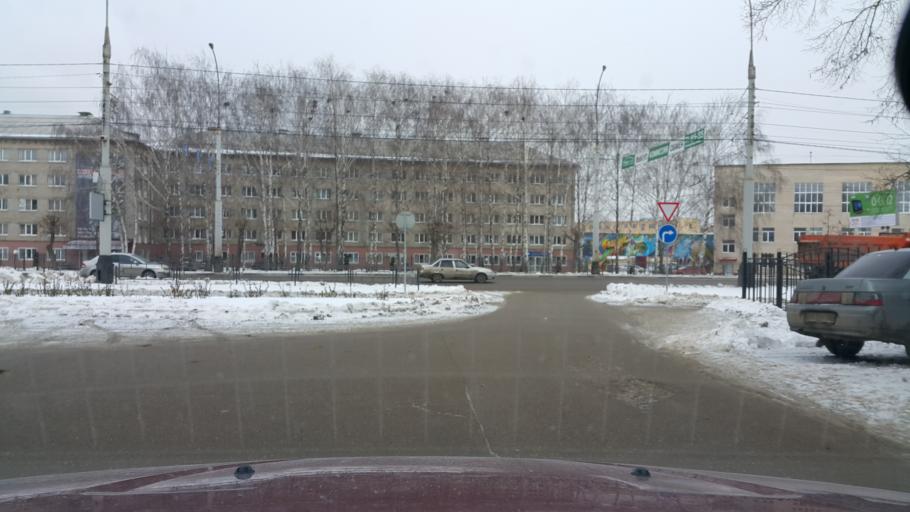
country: RU
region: Tambov
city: Tambov
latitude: 52.7449
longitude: 41.4494
